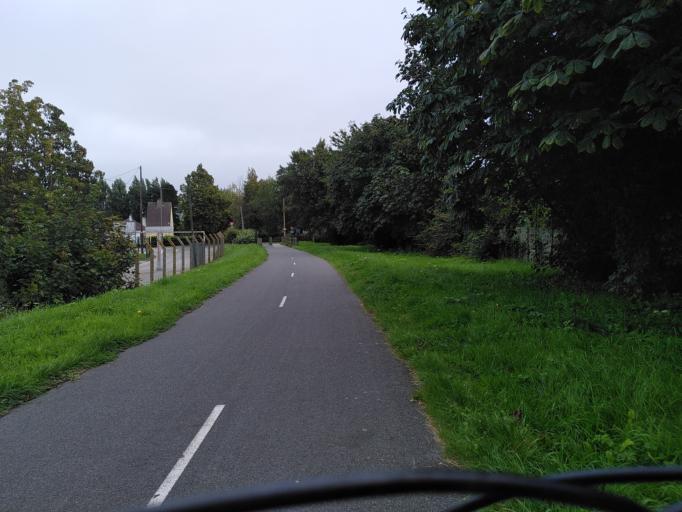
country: FR
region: Nord-Pas-de-Calais
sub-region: Departement du Pas-de-Calais
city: Aire-sur-la-Lys
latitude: 50.6417
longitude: 2.4049
